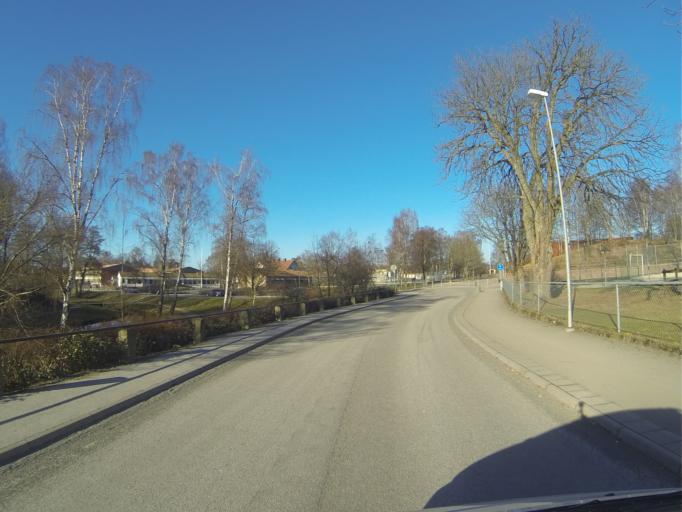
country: SE
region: Skane
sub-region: Hoors Kommun
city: Hoeoer
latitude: 55.9336
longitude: 13.5486
